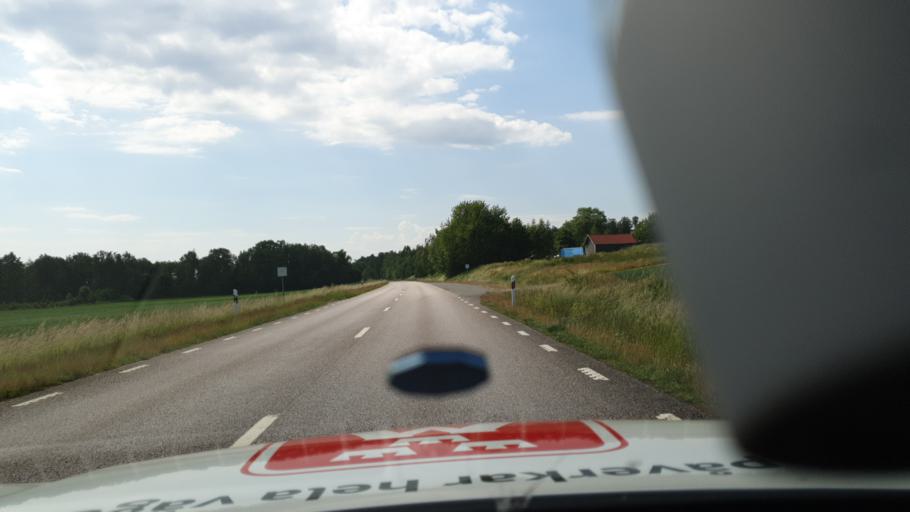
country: SE
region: Vaestra Goetaland
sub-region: Hjo Kommun
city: Hjo
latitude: 58.2131
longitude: 14.2047
